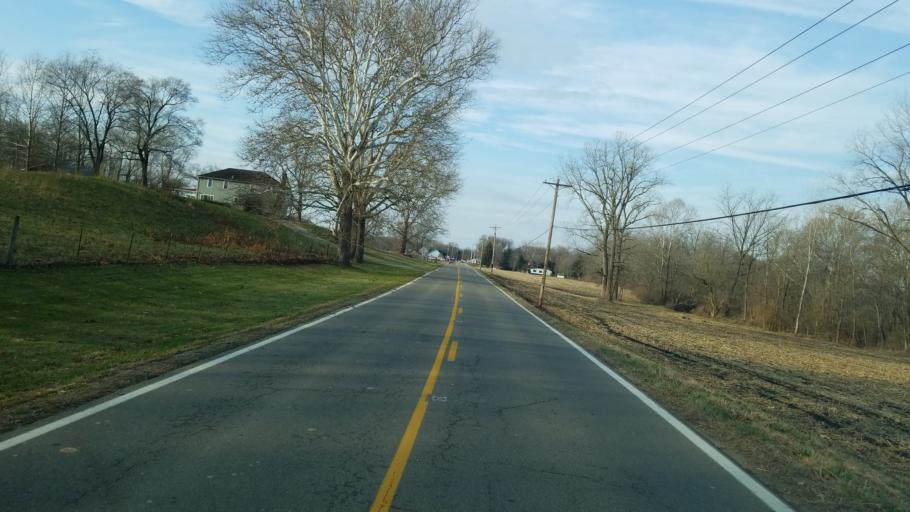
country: US
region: Ohio
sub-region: Ross County
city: Kingston
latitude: 39.4288
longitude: -82.9406
